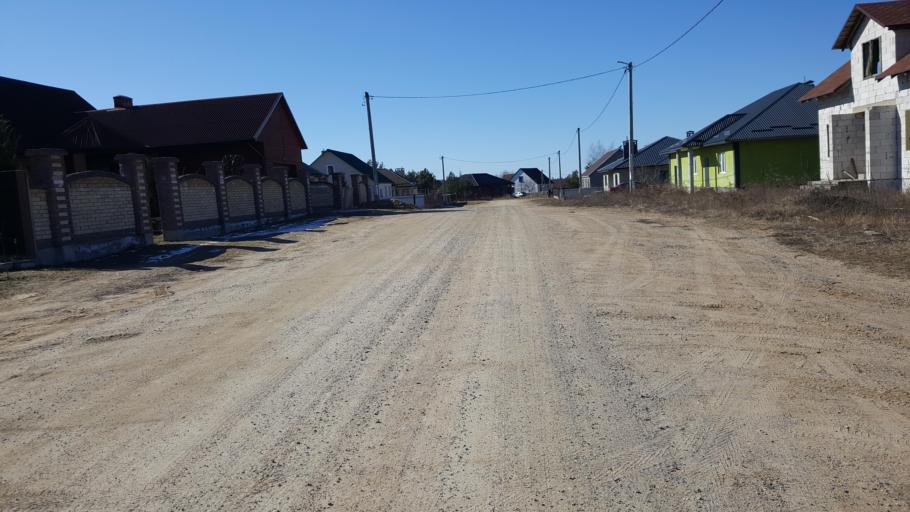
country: BY
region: Brest
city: Kamyanyets
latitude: 52.4052
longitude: 23.8418
